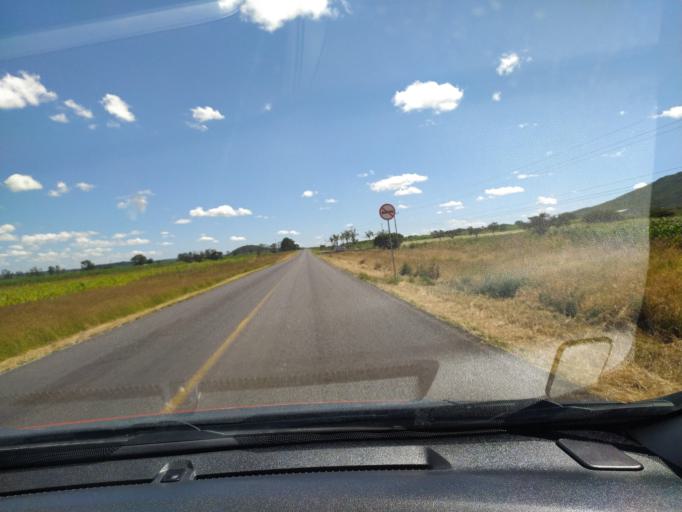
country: MX
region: Jalisco
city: San Miguel el Alto
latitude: 21.0166
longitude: -102.4717
